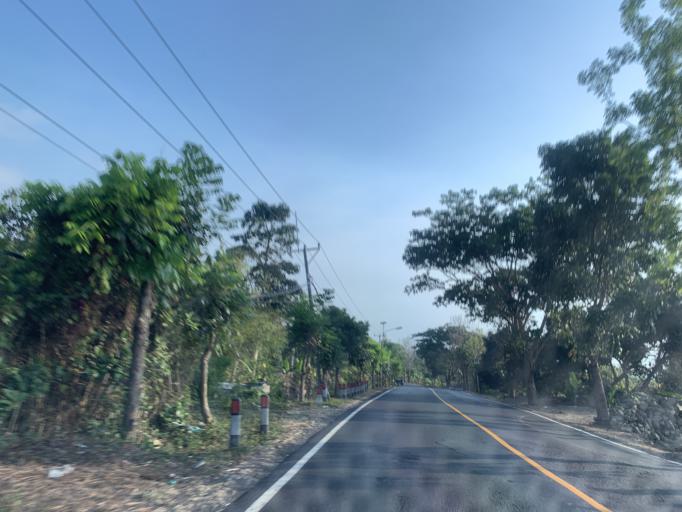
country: ID
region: Bali
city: Banjar Delodrurung
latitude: -8.5063
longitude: 115.0178
